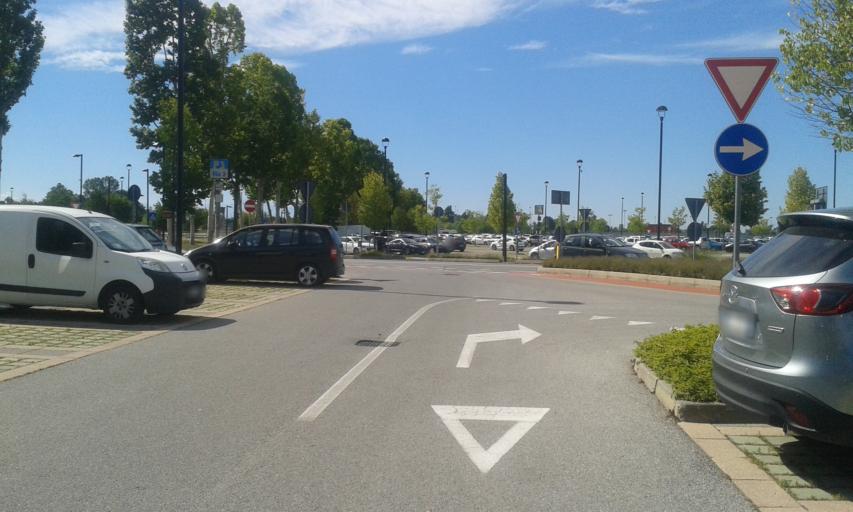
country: IT
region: Piedmont
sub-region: Provincia di Cuneo
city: Briaglia
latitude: 44.4208
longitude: 7.8534
